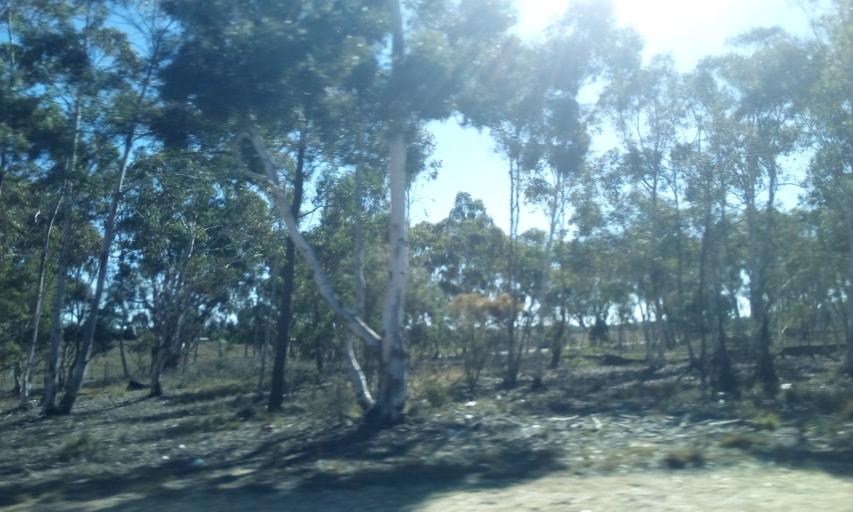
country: AU
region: New South Wales
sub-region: Yass Valley
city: Gundaroo
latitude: -35.1161
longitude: 149.3539
